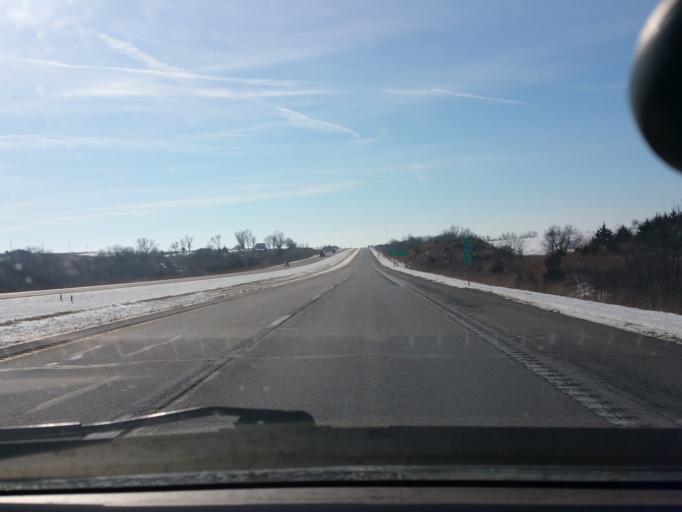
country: US
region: Iowa
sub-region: Decatur County
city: Lamoni
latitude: 40.5366
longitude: -93.9575
